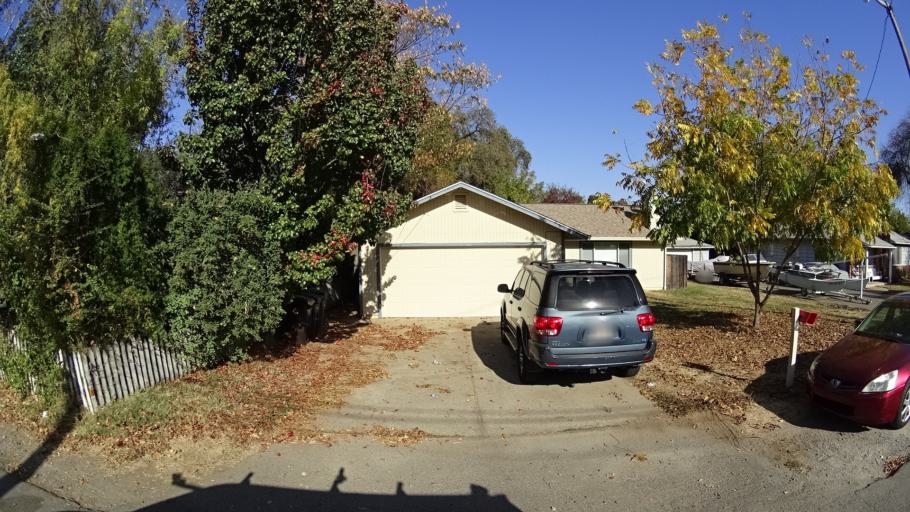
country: US
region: California
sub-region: Sacramento County
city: Citrus Heights
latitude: 38.6880
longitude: -121.2893
